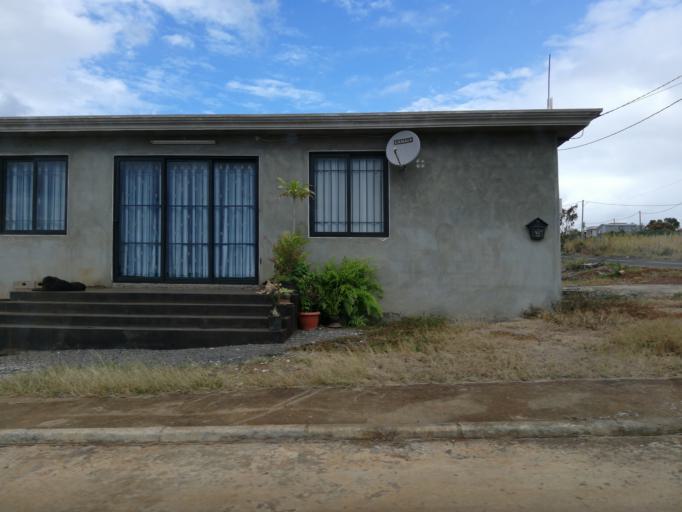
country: MU
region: Black River
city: Petite Riviere
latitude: -20.2140
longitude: 57.4629
